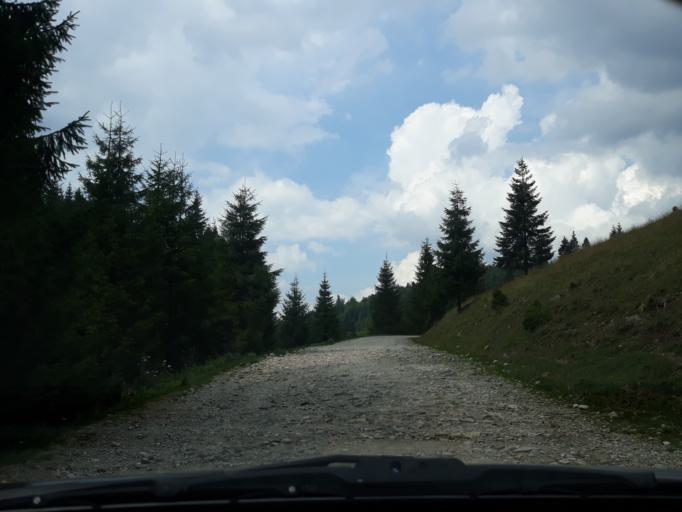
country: RO
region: Alba
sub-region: Comuna Arieseni
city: Arieseni
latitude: 46.5846
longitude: 22.6980
